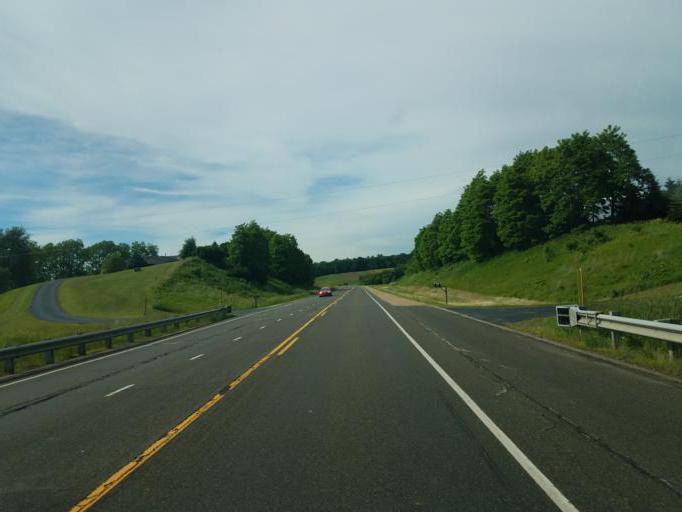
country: US
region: Wisconsin
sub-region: Monroe County
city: Tomah
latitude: 43.9146
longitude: -90.4945
